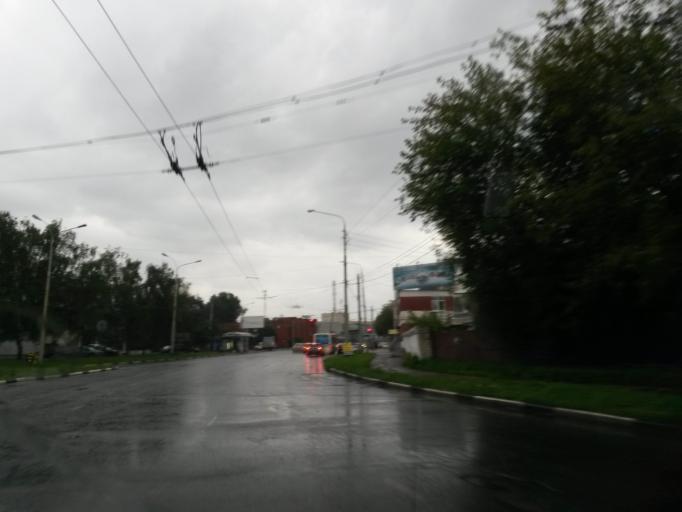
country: RU
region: Jaroslavl
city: Yaroslavl
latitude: 57.6444
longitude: 39.8813
